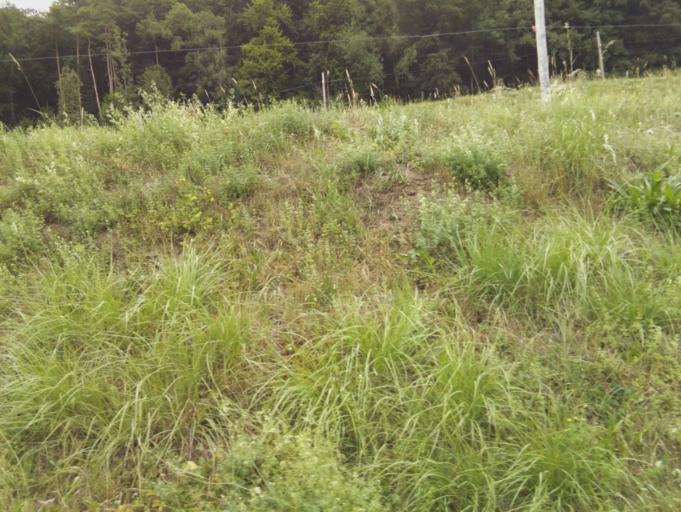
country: CH
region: Saint Gallen
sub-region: Wahlkreis Wil
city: Jonschwil
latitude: 47.4100
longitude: 9.0897
